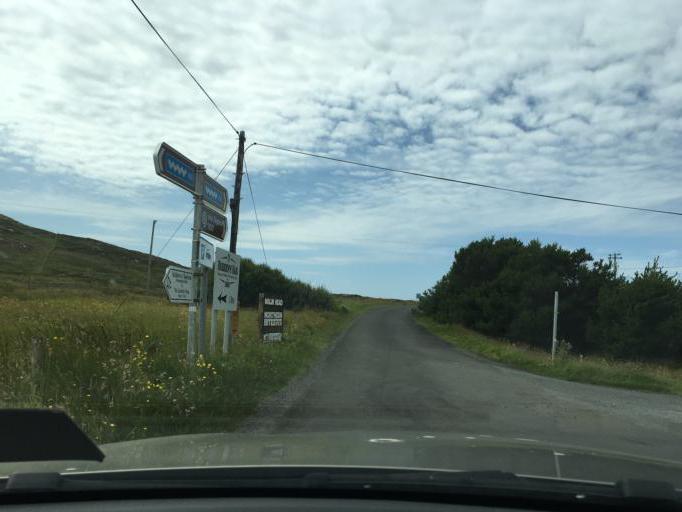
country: IE
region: Ulster
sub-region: County Donegal
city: Carndonagh
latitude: 55.3769
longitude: -7.3694
